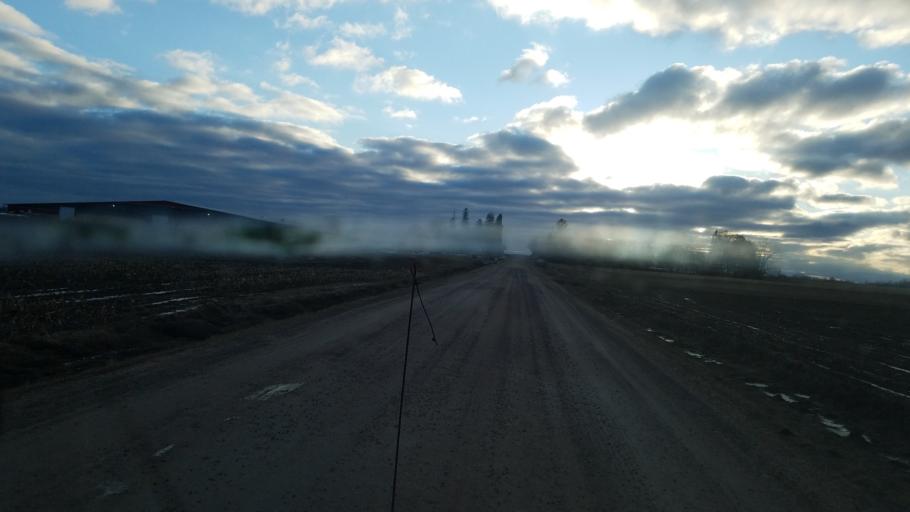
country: US
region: Wisconsin
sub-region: Clark County
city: Loyal
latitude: 44.6110
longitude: -90.4475
